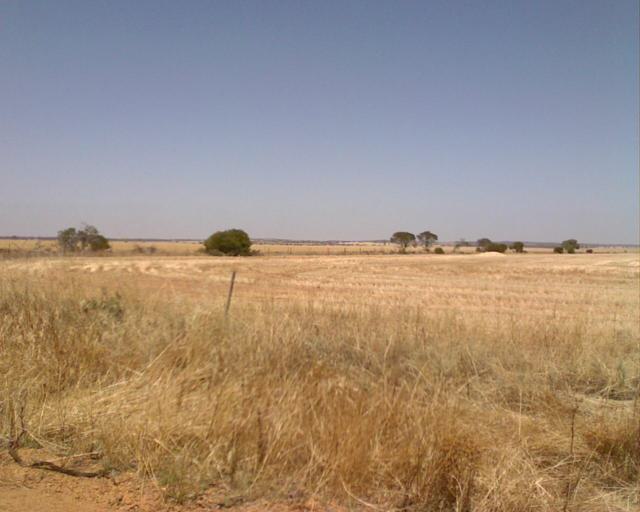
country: AU
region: Western Australia
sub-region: Merredin
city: Merredin
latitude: -30.8313
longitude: 118.2093
